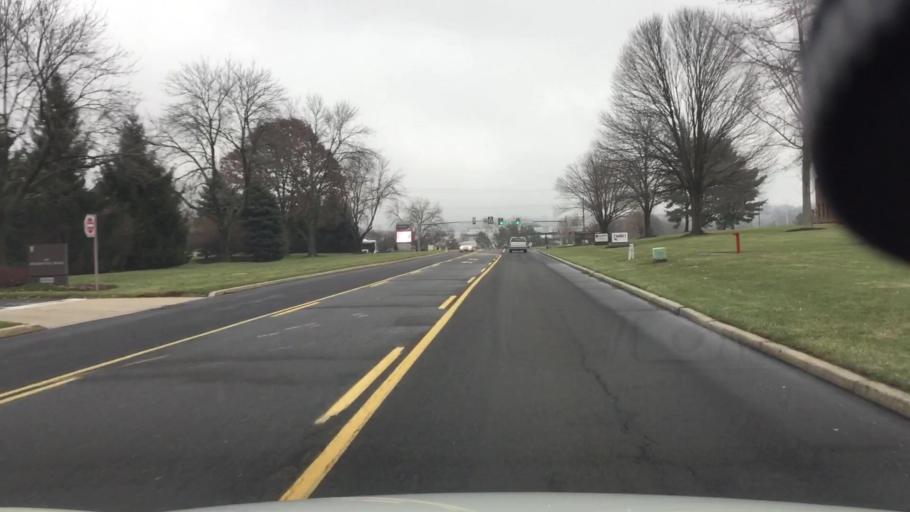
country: US
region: Pennsylvania
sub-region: Montgomery County
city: Horsham
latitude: 40.1691
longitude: -75.1406
